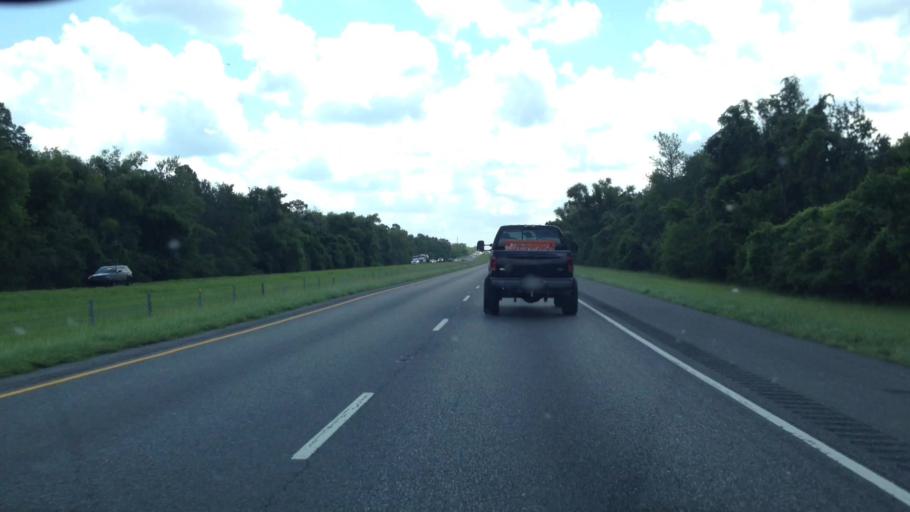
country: US
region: Louisiana
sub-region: Saint James Parish
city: Grand Point
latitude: 30.1338
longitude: -90.7273
